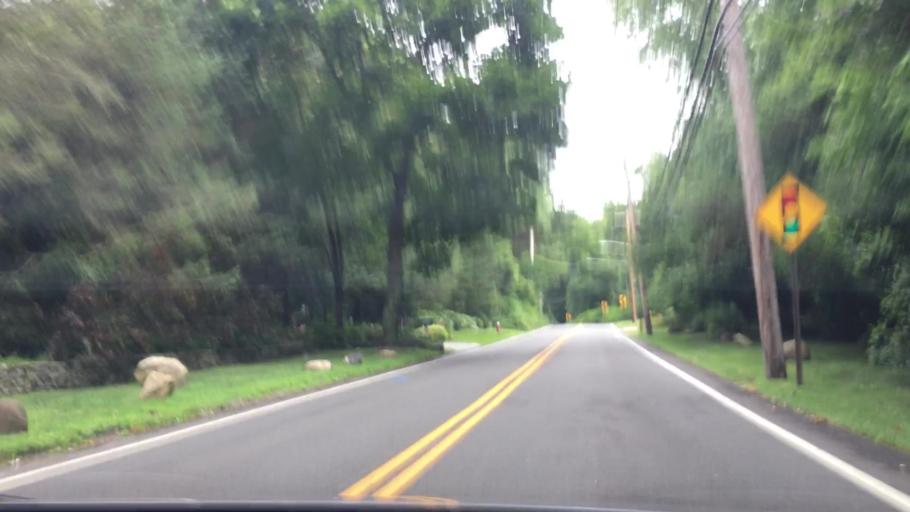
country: US
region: New York
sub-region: Suffolk County
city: West Hills
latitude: 40.8096
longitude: -73.4425
